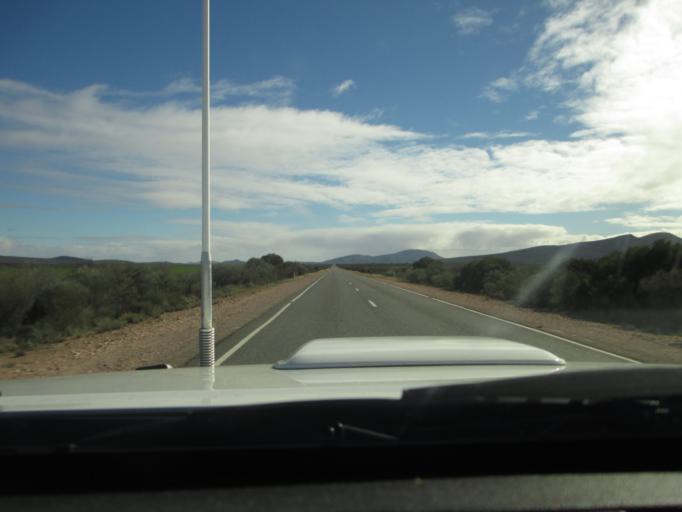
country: AU
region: South Australia
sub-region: Flinders Ranges
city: Quorn
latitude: -31.8703
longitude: 138.4082
